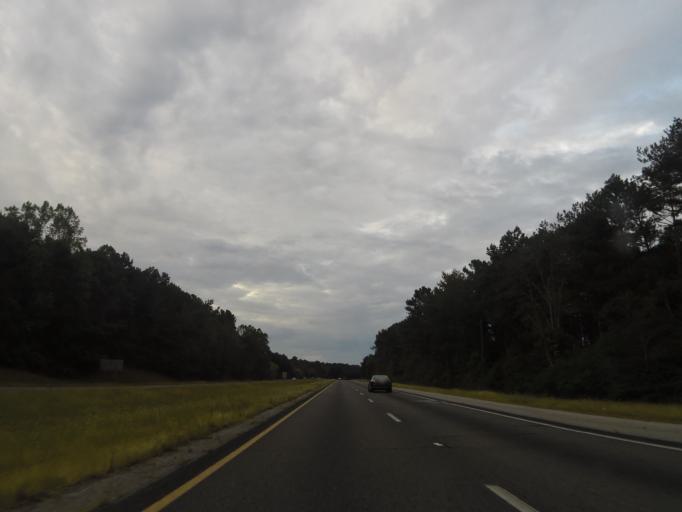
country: US
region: Alabama
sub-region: Jefferson County
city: Argo
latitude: 33.7083
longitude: -86.5210
